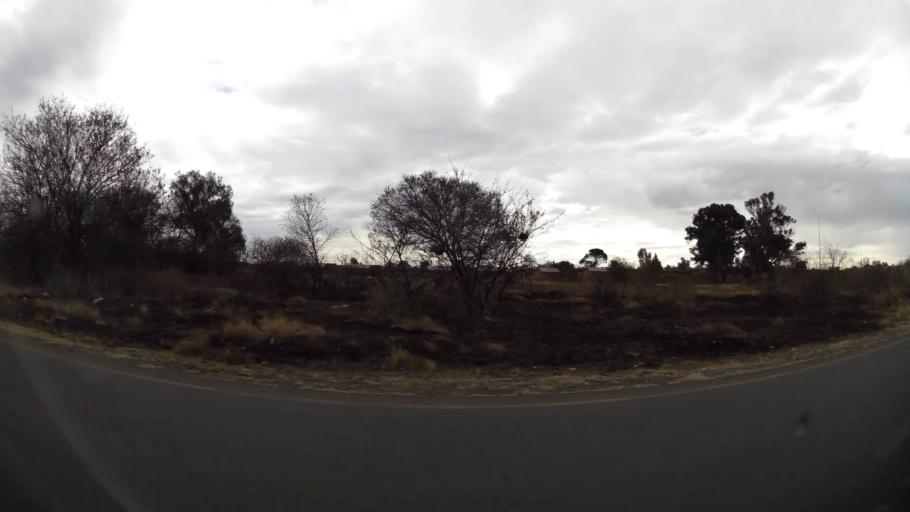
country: ZA
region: Orange Free State
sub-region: Fezile Dabi District Municipality
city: Kroonstad
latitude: -27.6528
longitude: 27.2266
